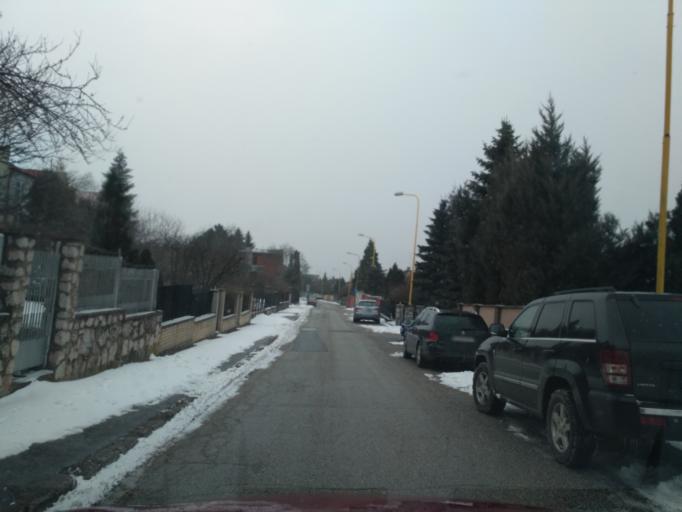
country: SK
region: Kosicky
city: Kosice
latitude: 48.7163
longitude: 21.2215
